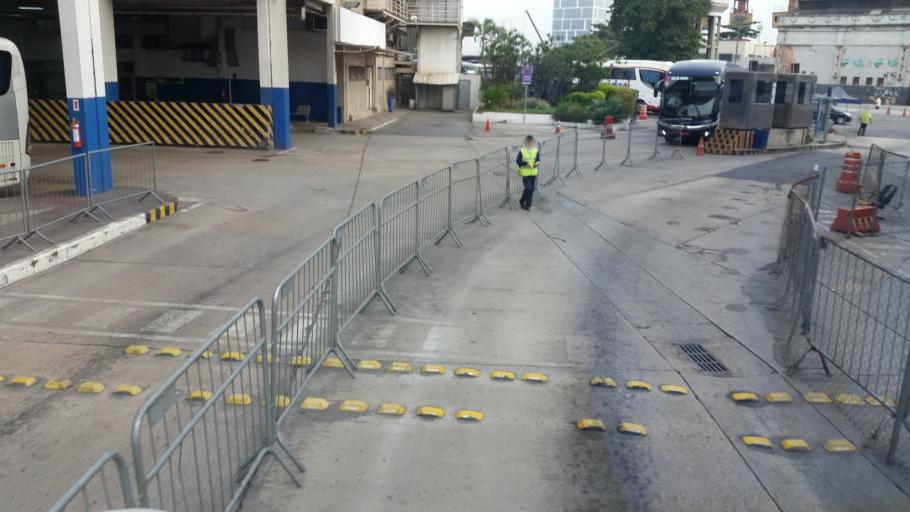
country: BR
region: Rio de Janeiro
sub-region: Rio De Janeiro
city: Rio de Janeiro
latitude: -22.8988
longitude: -43.2087
